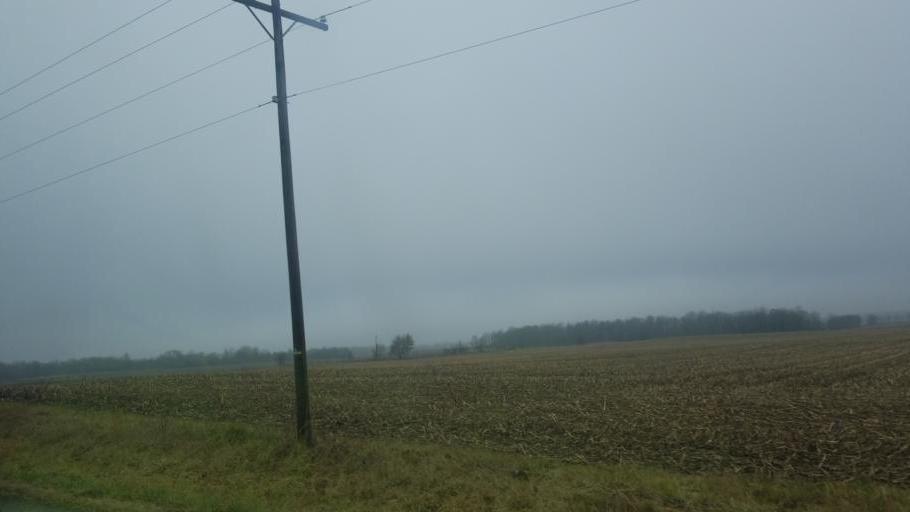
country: US
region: Ohio
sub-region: Champaign County
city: North Lewisburg
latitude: 40.2464
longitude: -83.5738
